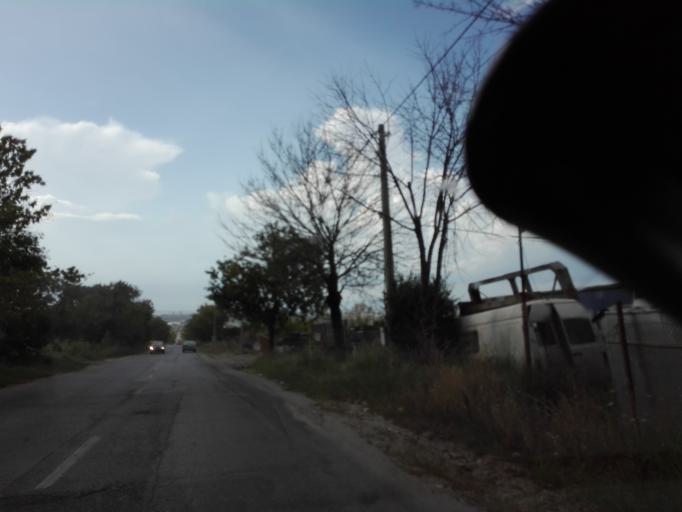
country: BG
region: Sofiya
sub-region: Obshtina Elin Pelin
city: Elin Pelin
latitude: 42.6091
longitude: 23.4670
